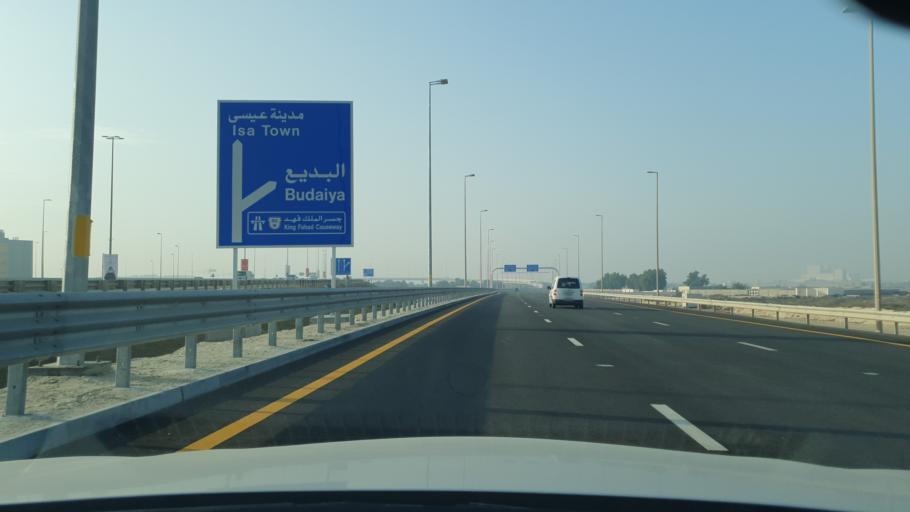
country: BH
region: Northern
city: Madinat `Isa
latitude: 26.1917
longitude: 50.5048
